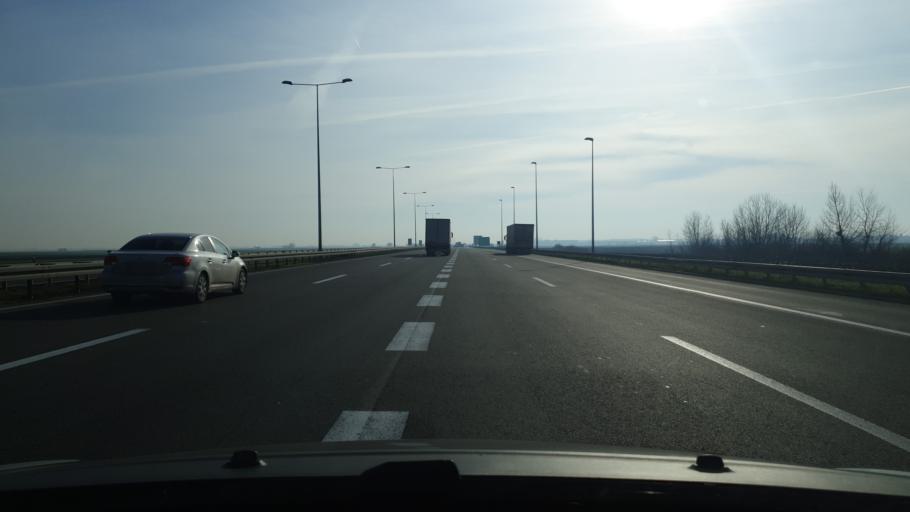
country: RS
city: Dobanovci
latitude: 44.8218
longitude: 20.2522
